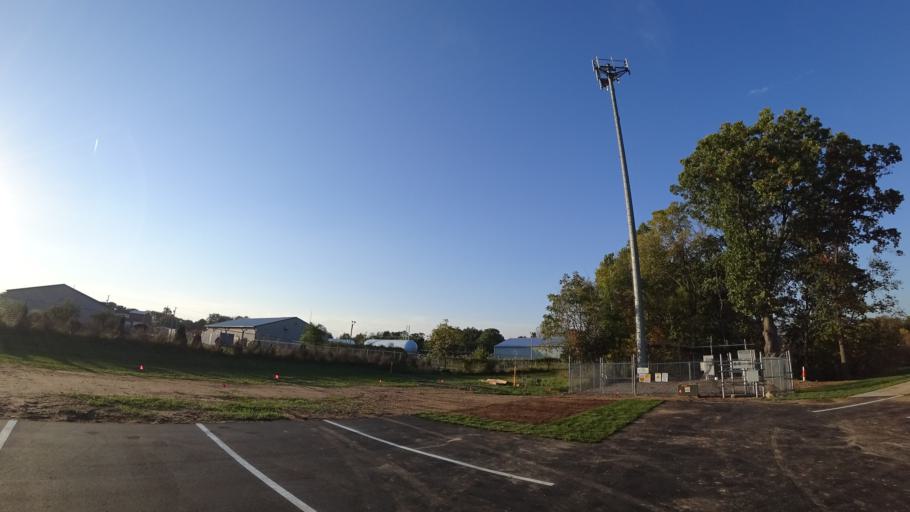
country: US
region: Michigan
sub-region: Saint Joseph County
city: Three Rivers
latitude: 41.9512
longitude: -85.6443
